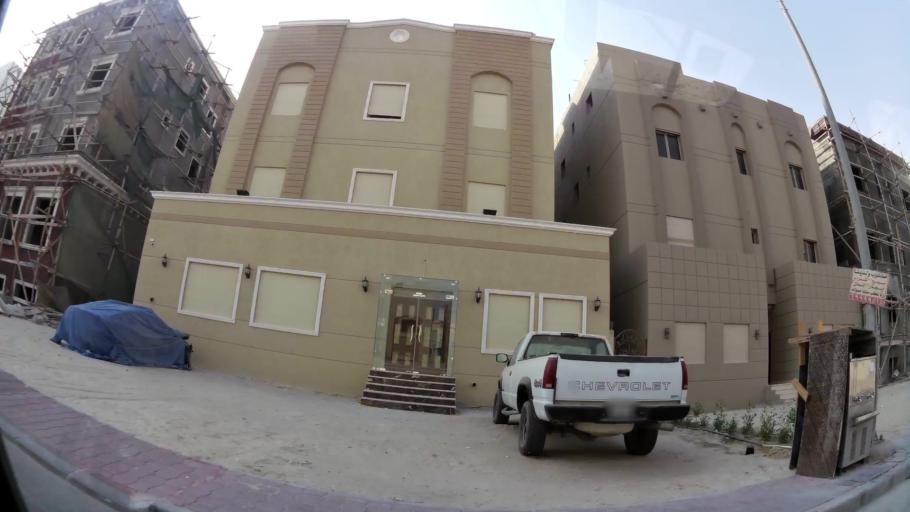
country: KW
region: Al Asimah
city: Ar Rabiyah
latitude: 29.3312
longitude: 47.8013
